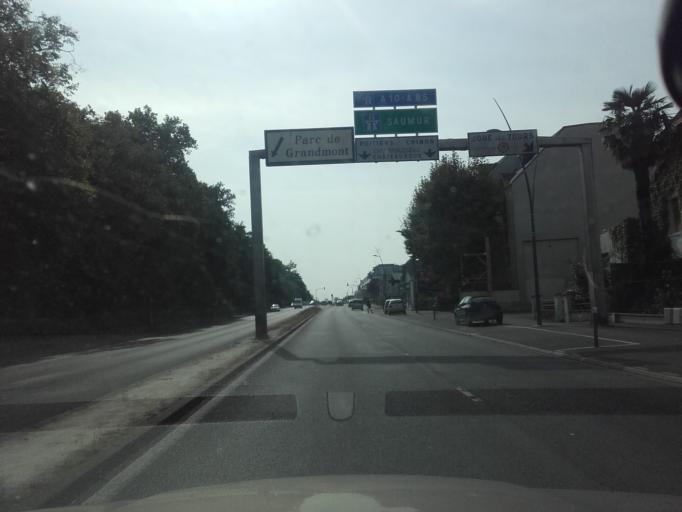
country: FR
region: Centre
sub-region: Departement d'Indre-et-Loire
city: Chambray-les-Tours
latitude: 47.3577
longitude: 0.6982
